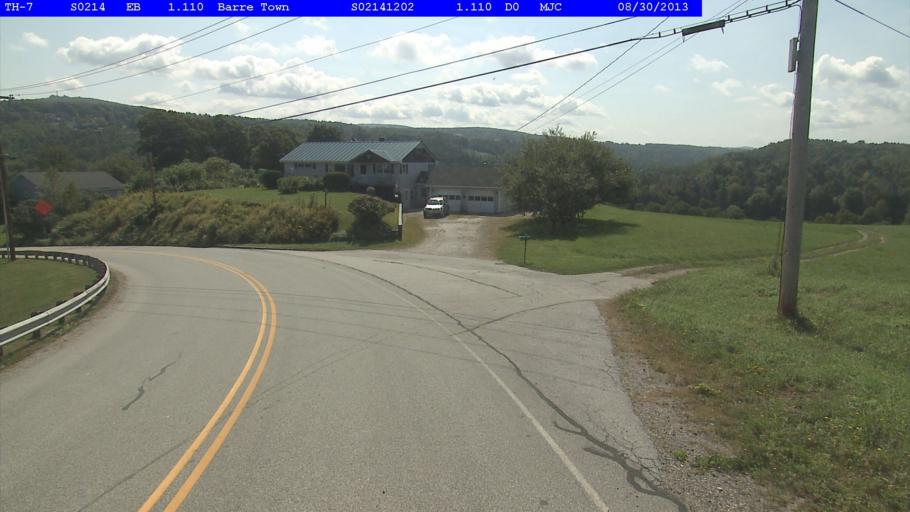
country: US
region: Vermont
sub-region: Washington County
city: South Barre
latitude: 44.1784
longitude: -72.5100
